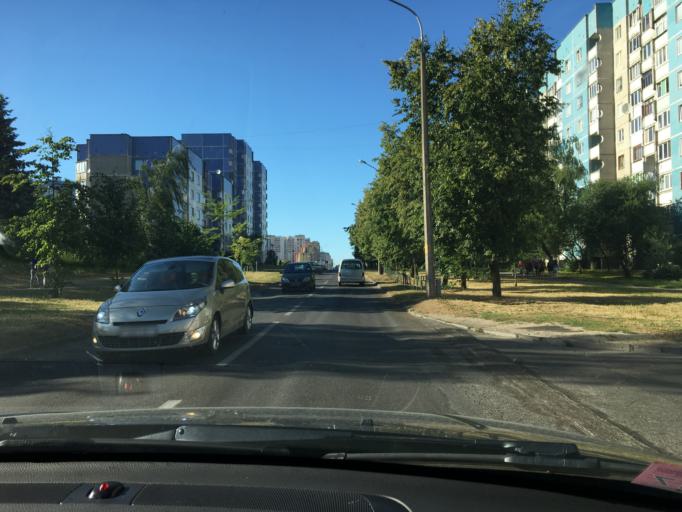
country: BY
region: Grodnenskaya
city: Hrodna
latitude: 53.7038
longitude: 23.8496
